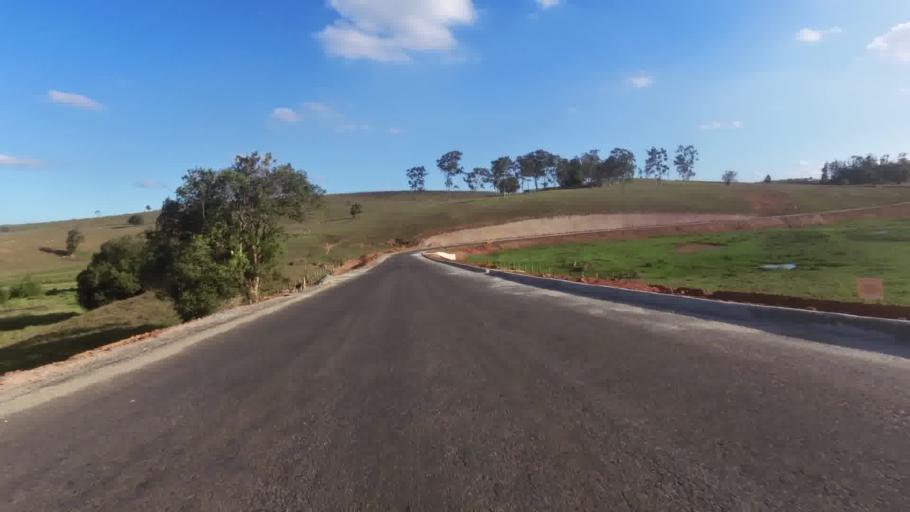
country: BR
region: Espirito Santo
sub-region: Marataizes
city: Marataizes
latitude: -21.1352
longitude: -41.0552
